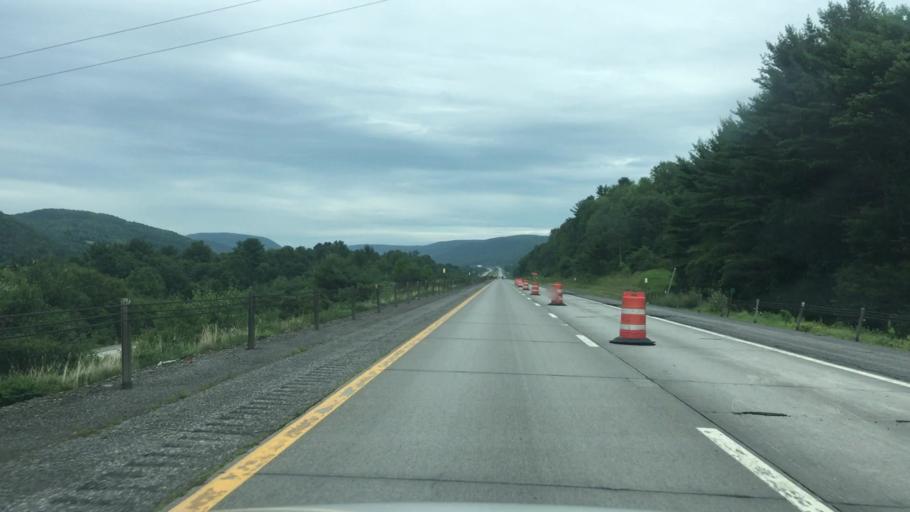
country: US
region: New York
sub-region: Otsego County
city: Worcester
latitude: 42.5302
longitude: -74.8760
